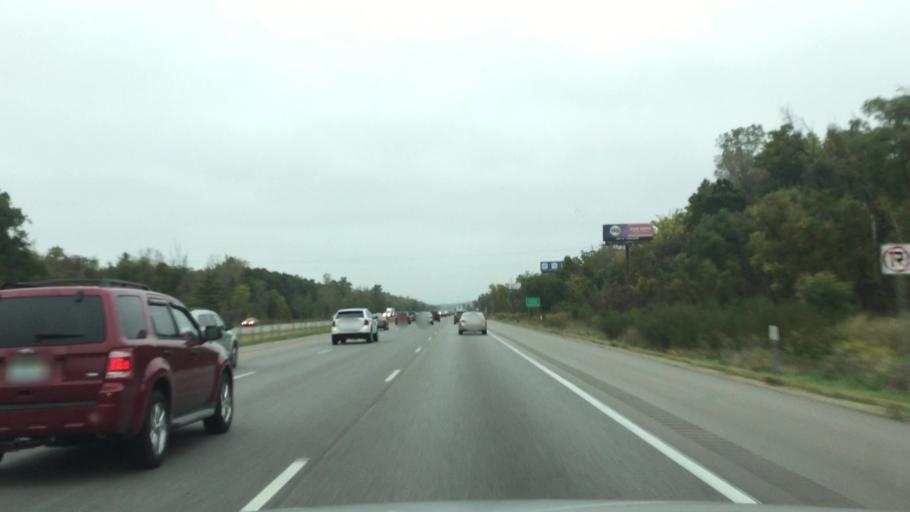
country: US
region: Michigan
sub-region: Berrien County
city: Stevensville
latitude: 41.9843
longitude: -86.5418
